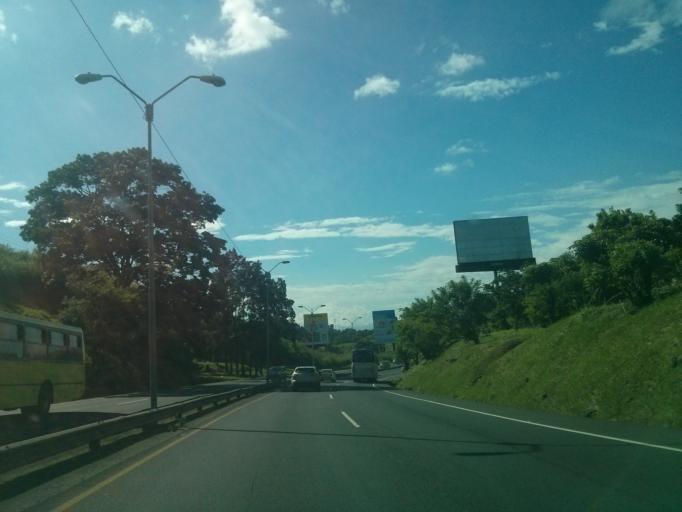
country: CR
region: San Jose
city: Colima
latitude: 9.9432
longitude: -84.1033
